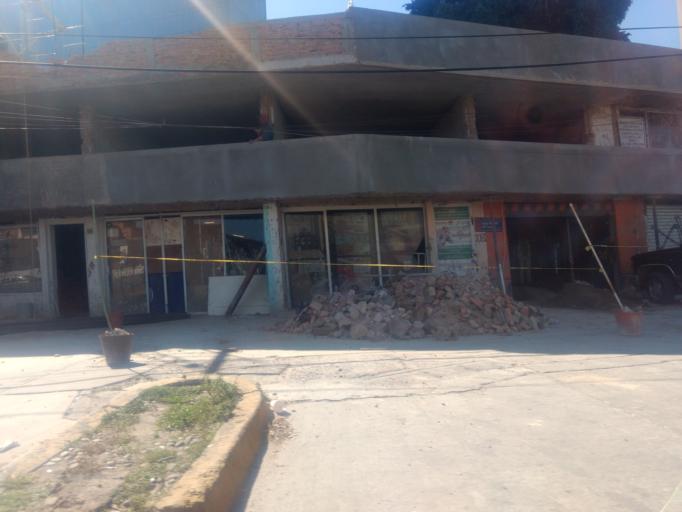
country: MX
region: Jalisco
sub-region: Zapopan
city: Zapopan
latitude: 20.6973
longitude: -103.3715
